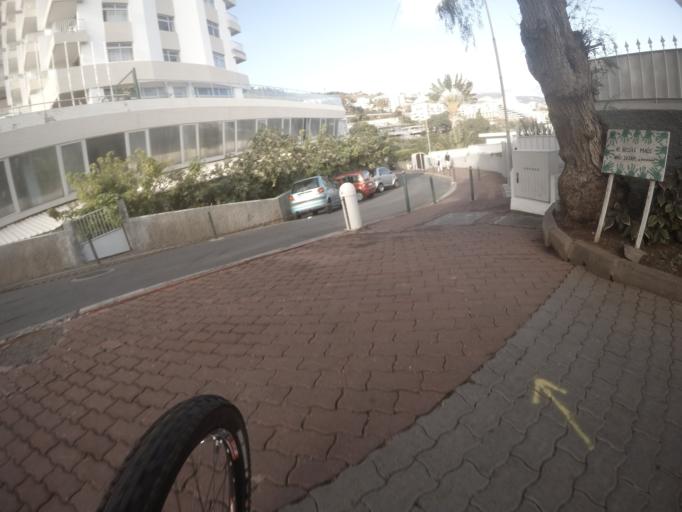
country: PT
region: Madeira
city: Camara de Lobos
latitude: 32.6351
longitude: -16.9397
